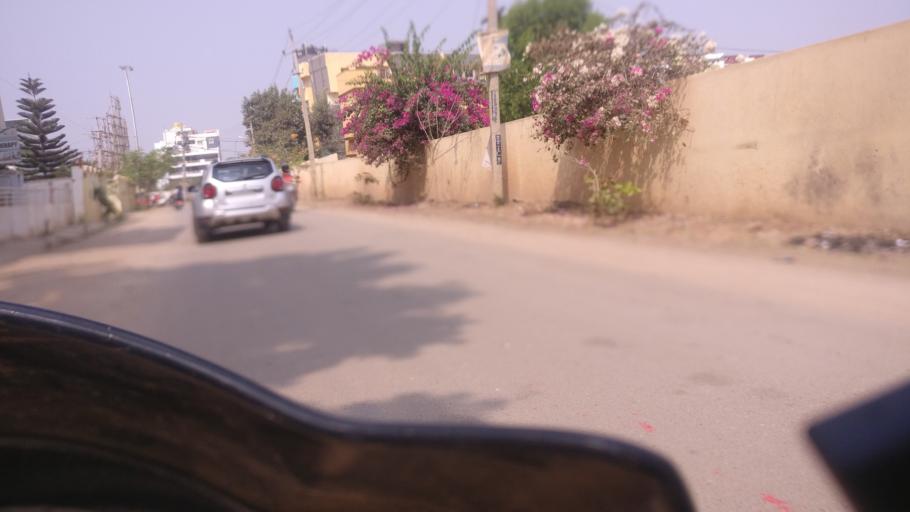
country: IN
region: Karnataka
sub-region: Bangalore Urban
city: Bangalore
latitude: 12.9024
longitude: 77.6861
